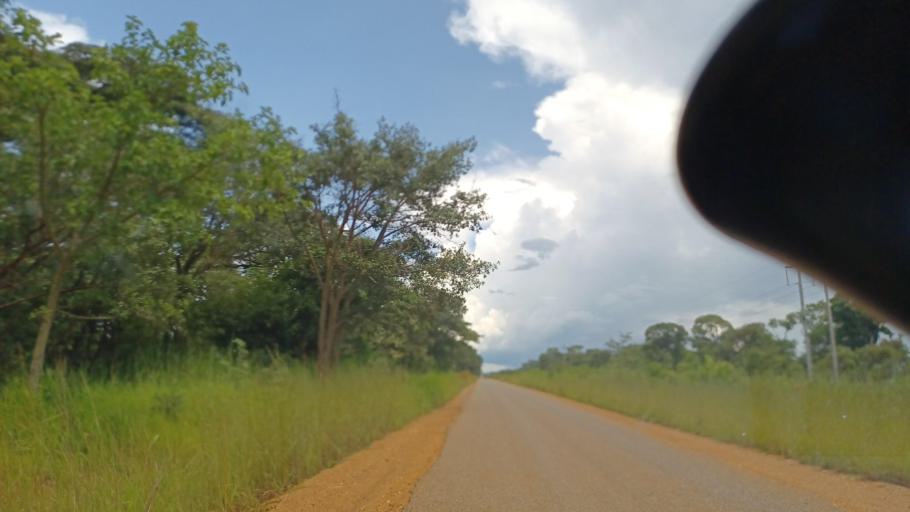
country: ZM
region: North-Western
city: Kasempa
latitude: -12.8753
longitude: 26.0430
